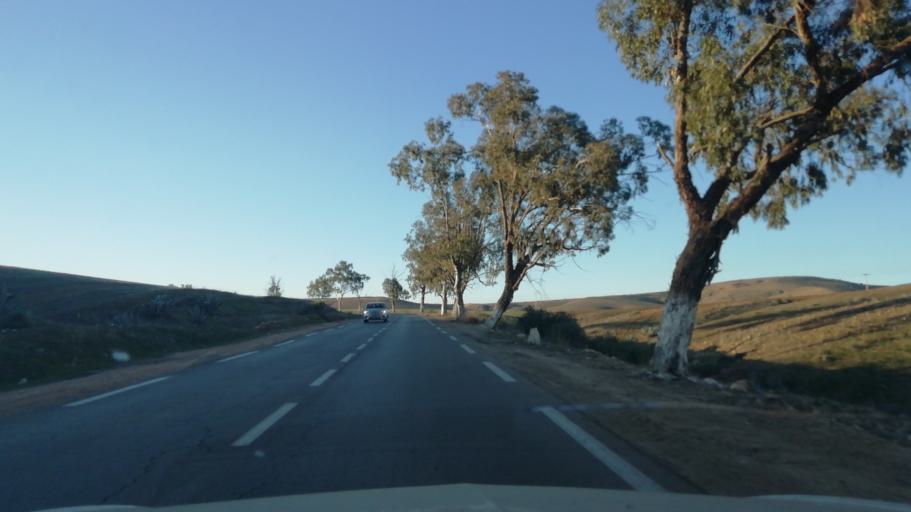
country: DZ
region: Tlemcen
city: Nedroma
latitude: 34.8293
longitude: -1.6641
